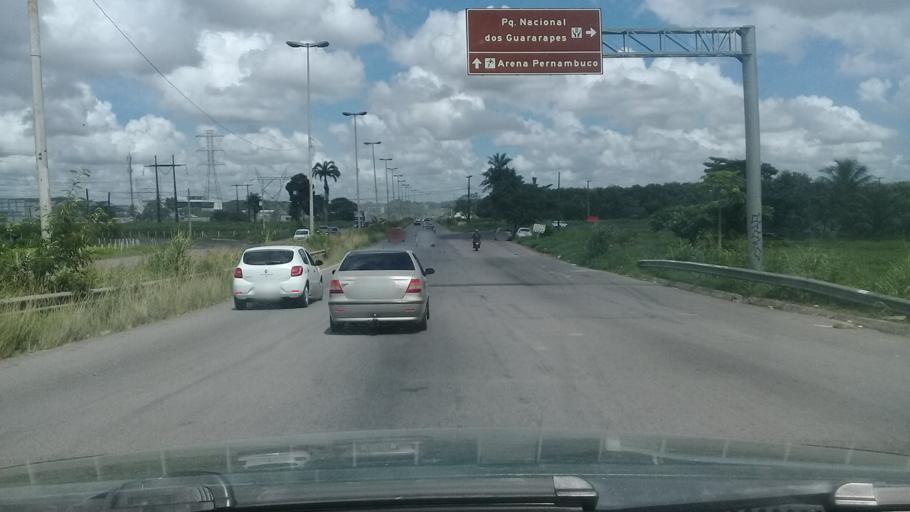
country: BR
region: Pernambuco
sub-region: Recife
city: Recife
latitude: -8.0676
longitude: -34.9444
